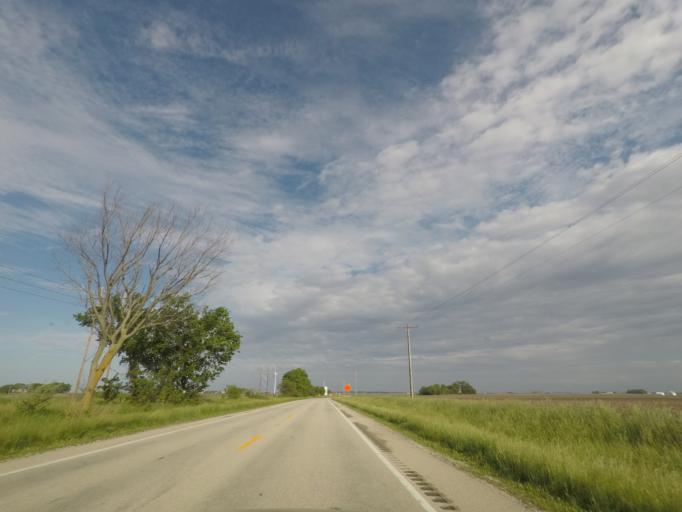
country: US
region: Illinois
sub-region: Logan County
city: Mount Pulaski
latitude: 39.9824
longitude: -89.2137
